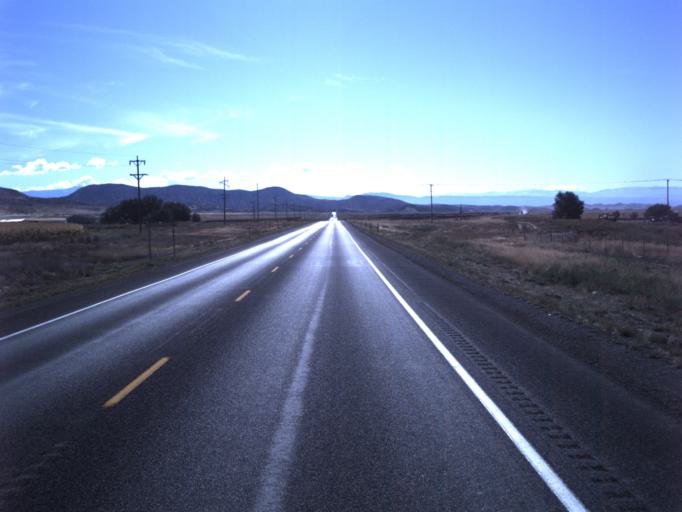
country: US
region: Utah
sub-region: Sanpete County
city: Gunnison
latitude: 39.2645
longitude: -111.8678
